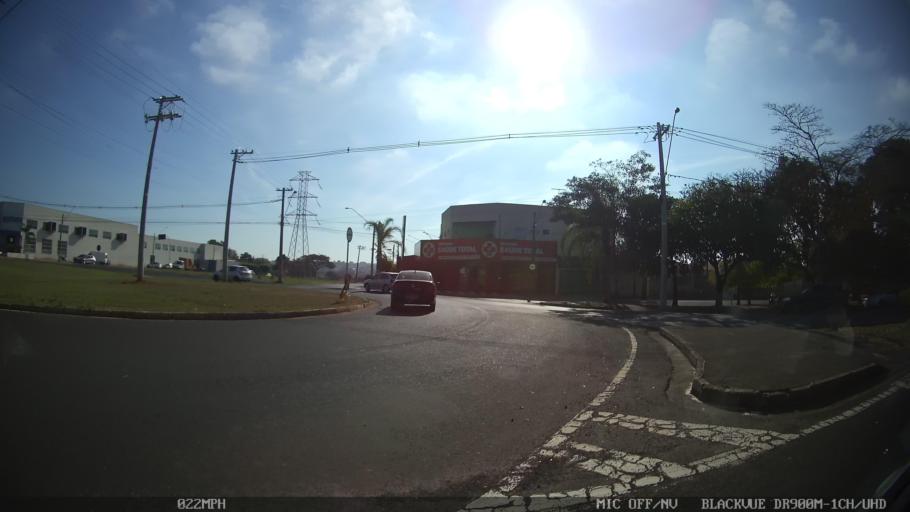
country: BR
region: Sao Paulo
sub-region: Sao Jose Do Rio Preto
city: Sao Jose do Rio Preto
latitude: -20.7943
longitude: -49.4149
